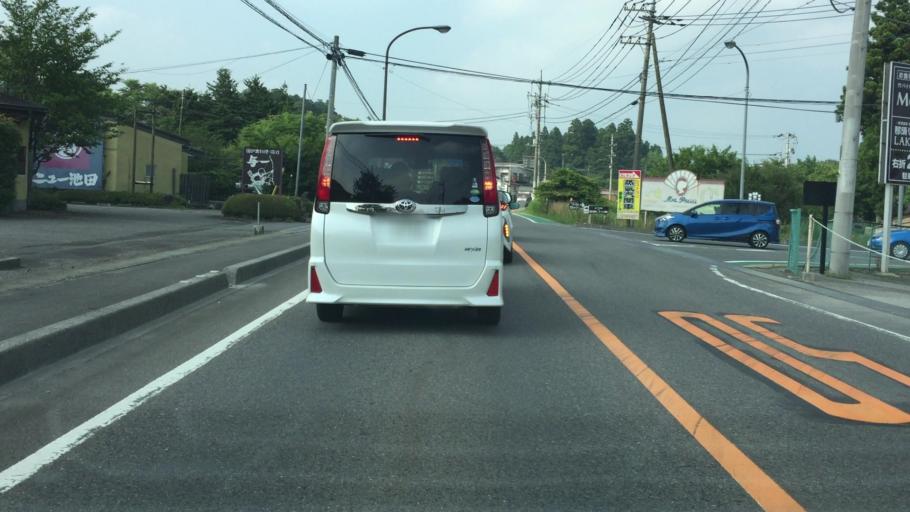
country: JP
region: Tochigi
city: Kuroiso
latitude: 37.0552
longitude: 140.0361
